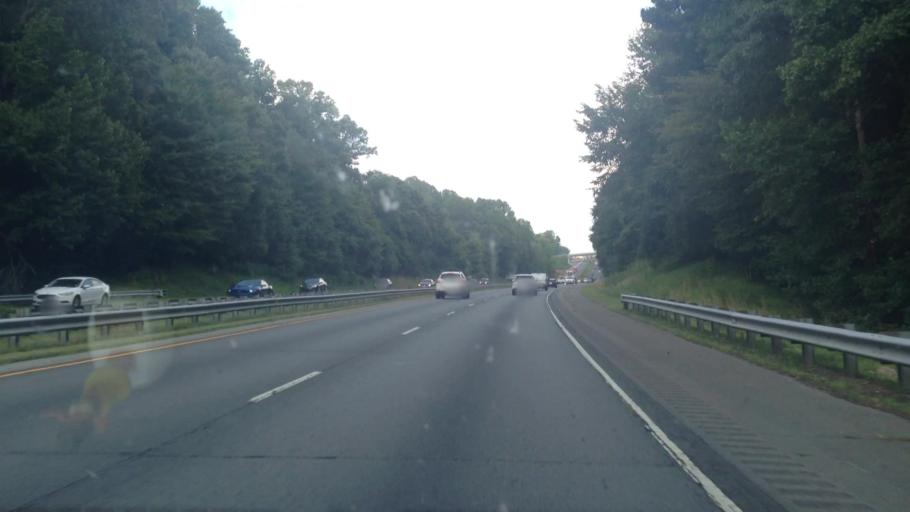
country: US
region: North Carolina
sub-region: Forsyth County
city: Walkertown
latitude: 36.1140
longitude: -80.1545
